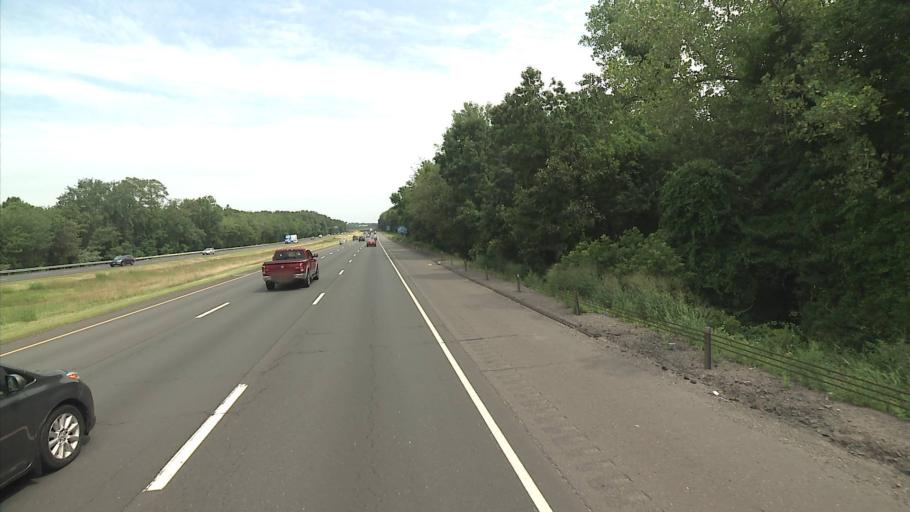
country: US
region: Connecticut
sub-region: New Haven County
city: Wolcott
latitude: 41.5982
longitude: -72.9028
